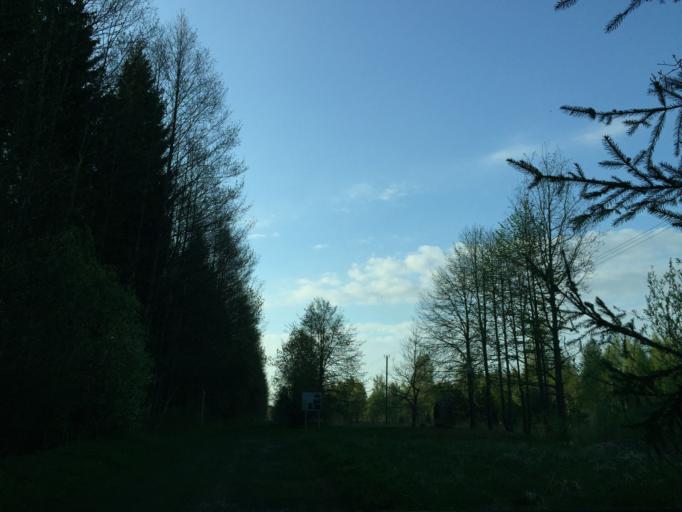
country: LV
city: Tireli
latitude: 56.8475
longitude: 23.7148
